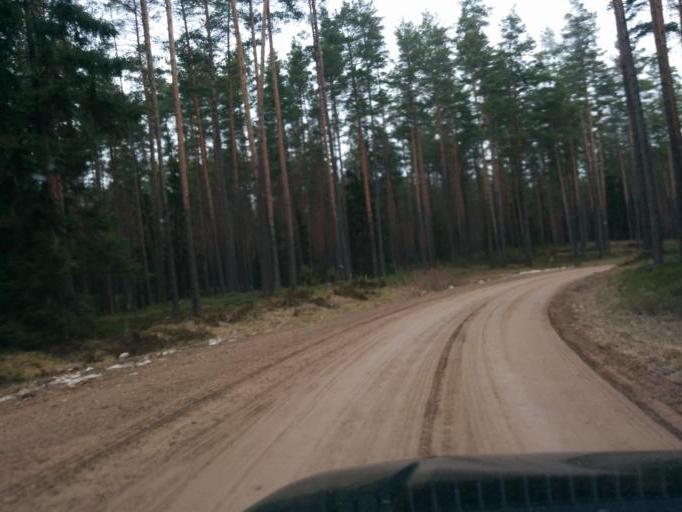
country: LV
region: Ogre
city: Ogre
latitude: 56.7771
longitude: 24.6033
